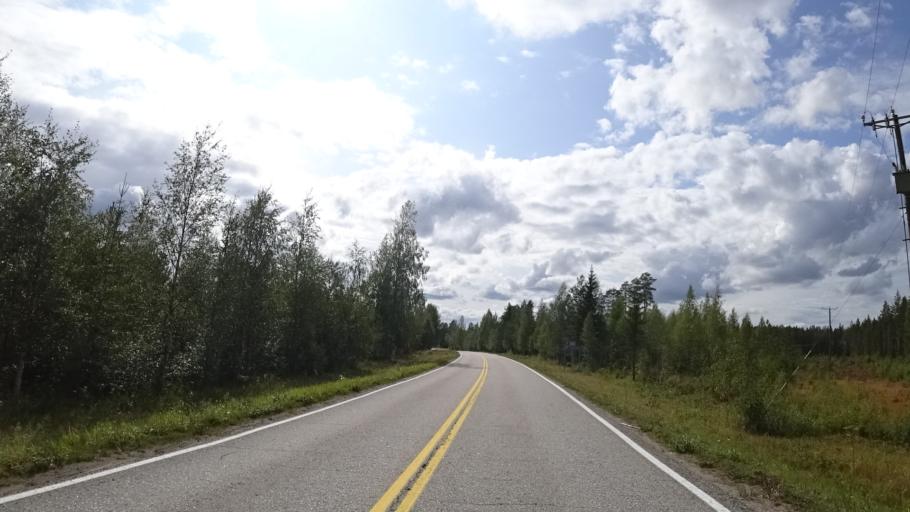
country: FI
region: North Karelia
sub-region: Joensuu
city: Ilomantsi
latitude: 62.7681
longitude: 31.0383
